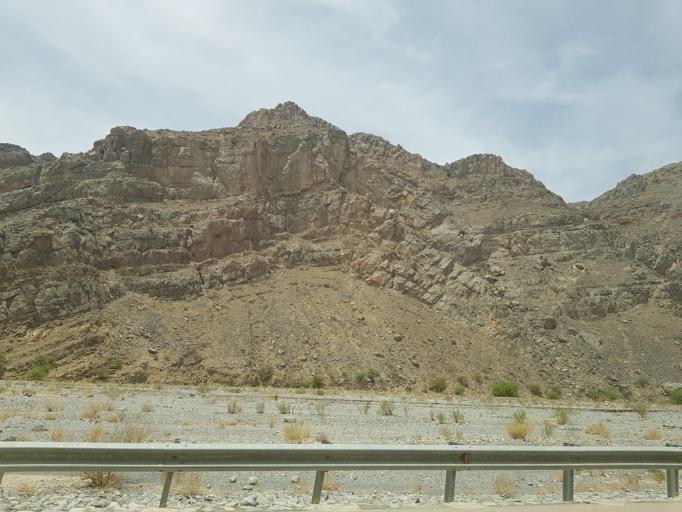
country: OM
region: Muhafazat ad Dakhiliyah
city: Izki
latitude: 22.9324
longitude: 57.6688
